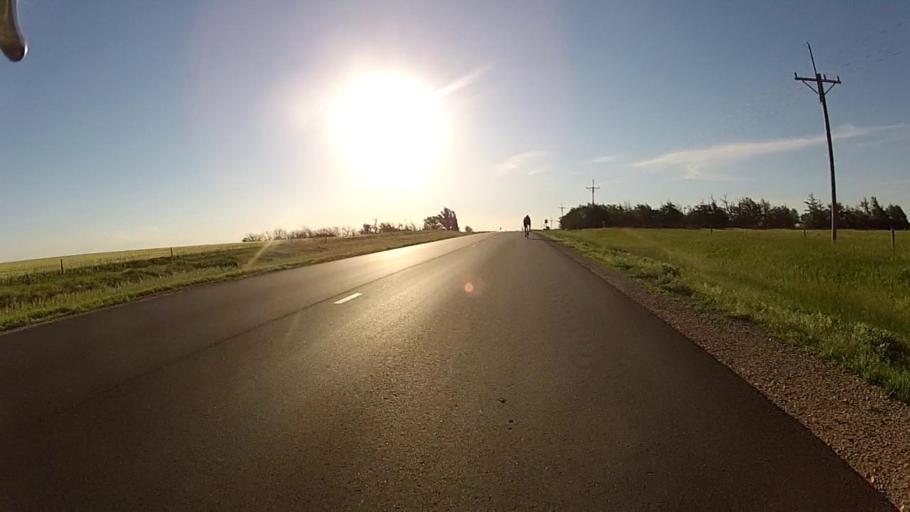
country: US
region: Kansas
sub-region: Comanche County
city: Coldwater
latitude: 37.2817
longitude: -99.1516
